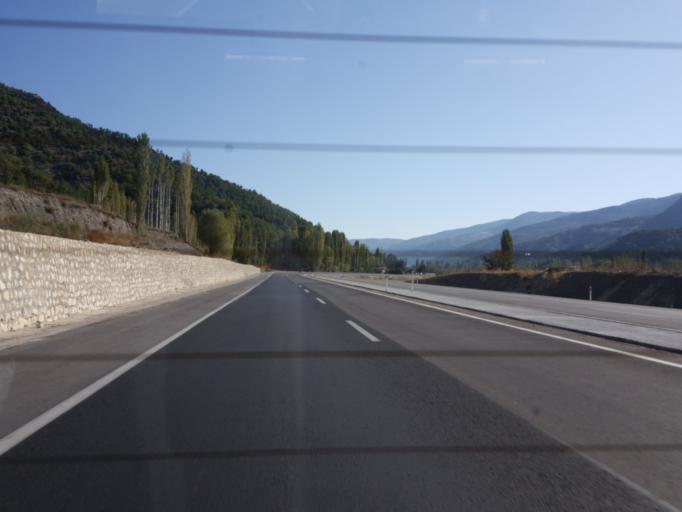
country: TR
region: Tokat
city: Turhal
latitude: 40.4736
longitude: 36.1359
